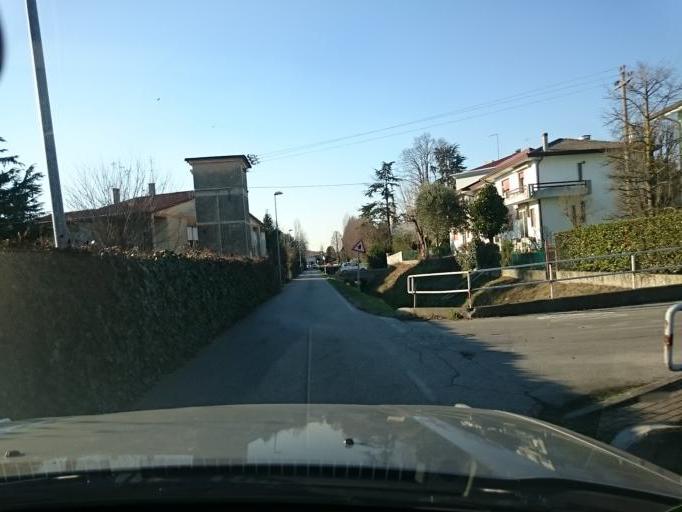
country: IT
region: Veneto
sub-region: Provincia di Venezia
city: Dolo
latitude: 45.4225
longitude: 12.0819
